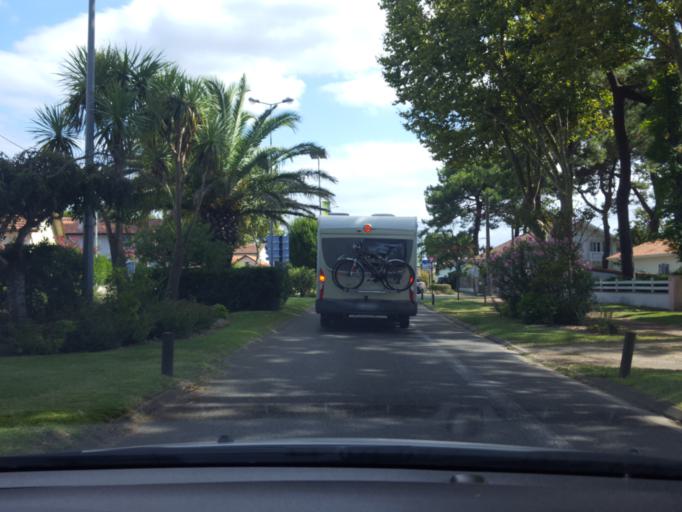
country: FR
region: Aquitaine
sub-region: Departement des Landes
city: Capbreton
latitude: 43.6442
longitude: -1.4266
